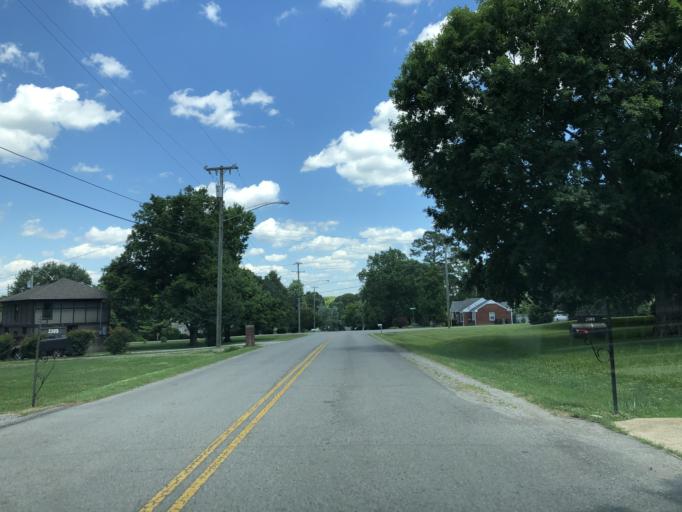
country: US
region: Tennessee
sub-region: Davidson County
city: Nashville
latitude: 36.1806
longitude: -86.7246
